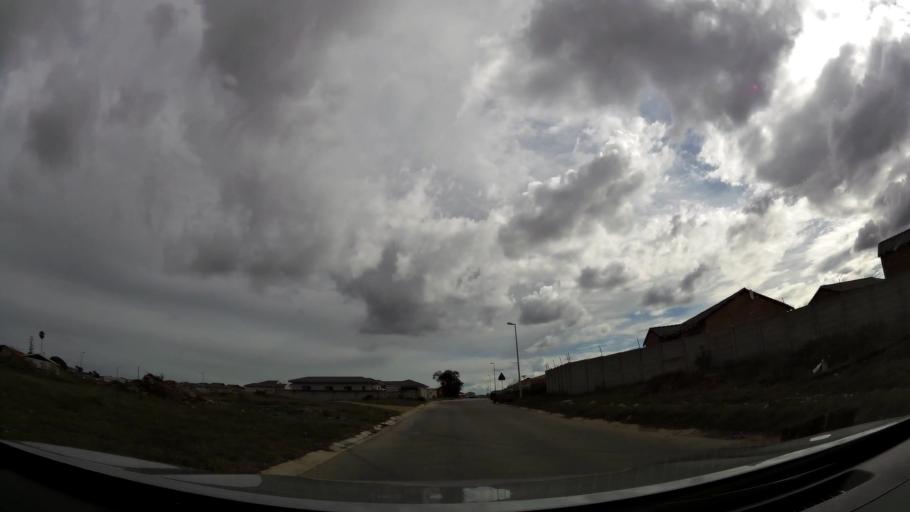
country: ZA
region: Eastern Cape
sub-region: Nelson Mandela Bay Metropolitan Municipality
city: Port Elizabeth
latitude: -33.9316
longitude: 25.5056
